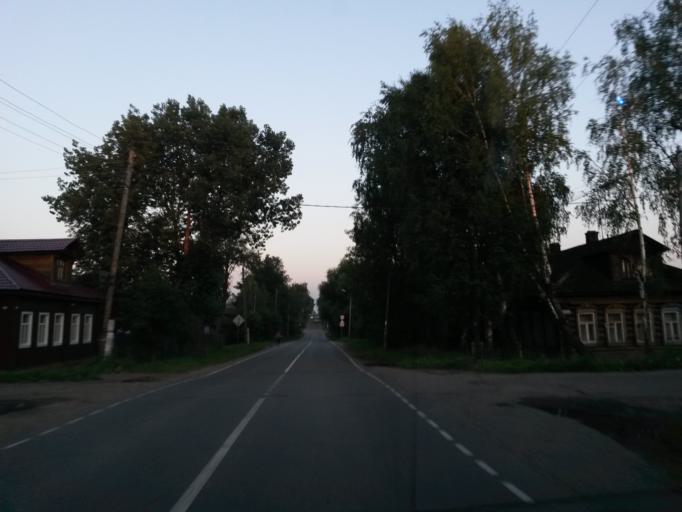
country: RU
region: Jaroslavl
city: Tutayev
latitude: 57.8884
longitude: 39.5372
